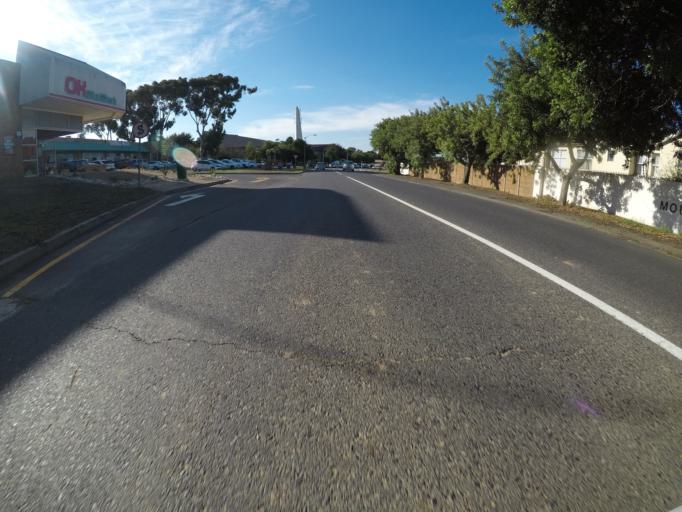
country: ZA
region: Western Cape
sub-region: City of Cape Town
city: Kraaifontein
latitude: -33.8760
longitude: 18.6454
